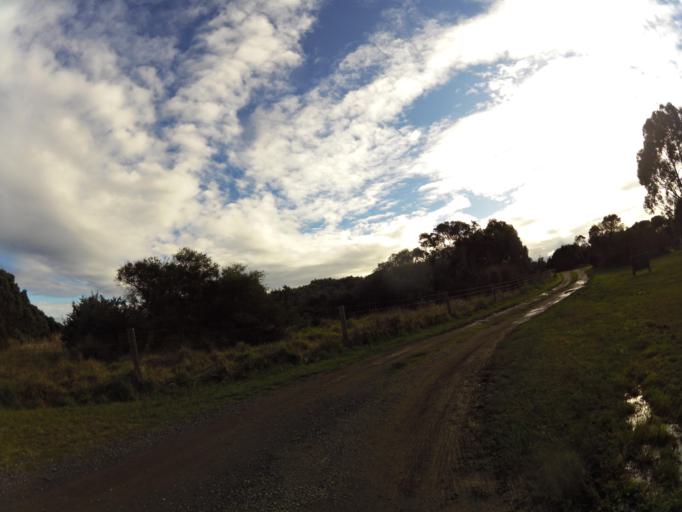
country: AU
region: Victoria
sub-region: Bass Coast
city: North Wonthaggi
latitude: -38.6170
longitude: 145.5762
